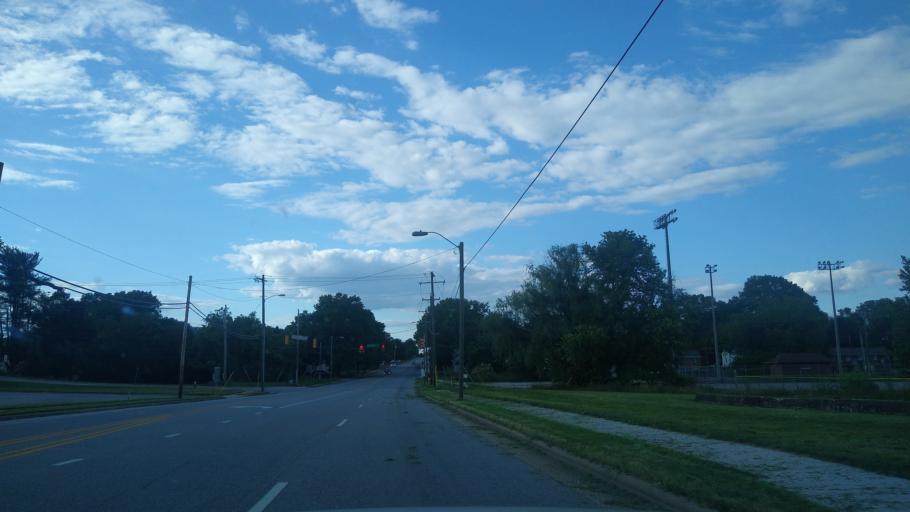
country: US
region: North Carolina
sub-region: Guilford County
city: Greensboro
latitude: 36.1009
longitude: -79.7752
